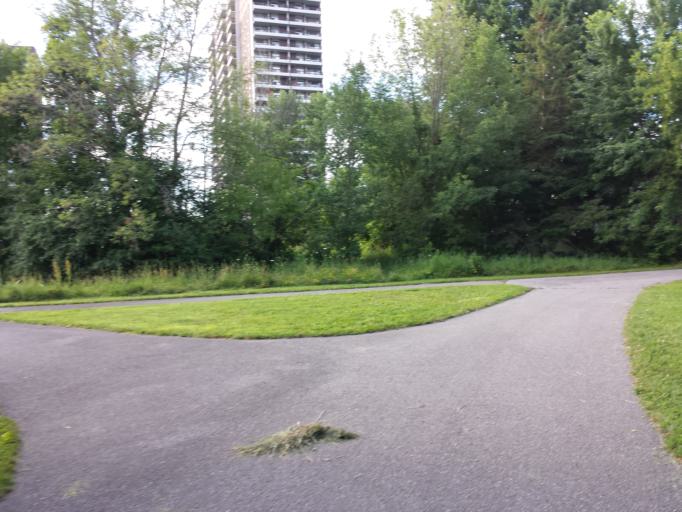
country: CA
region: Ontario
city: Bells Corners
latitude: 45.3701
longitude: -75.7863
